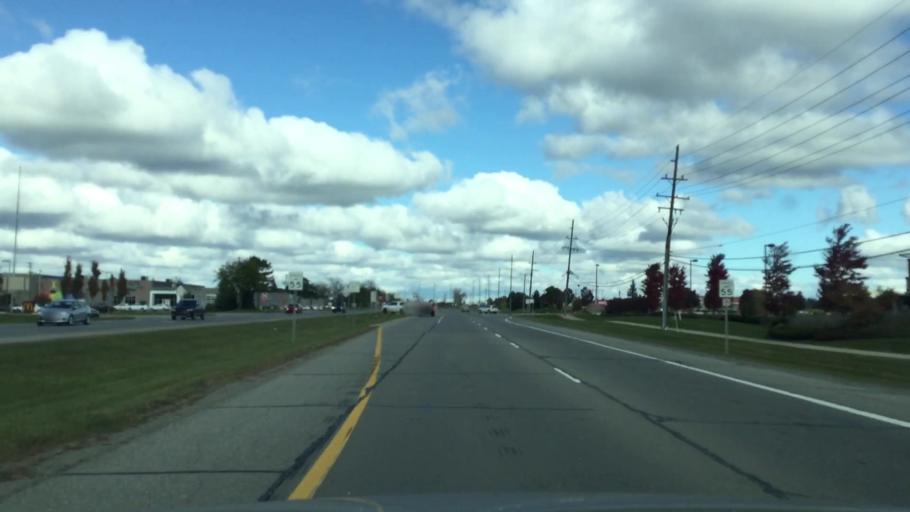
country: US
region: Michigan
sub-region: Oakland County
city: Oxford
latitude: 42.8364
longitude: -83.2720
